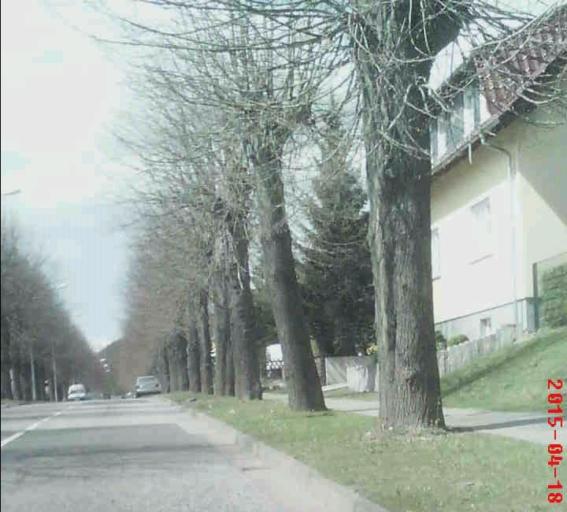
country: DE
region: Thuringia
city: Worbis
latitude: 51.4247
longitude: 10.3573
